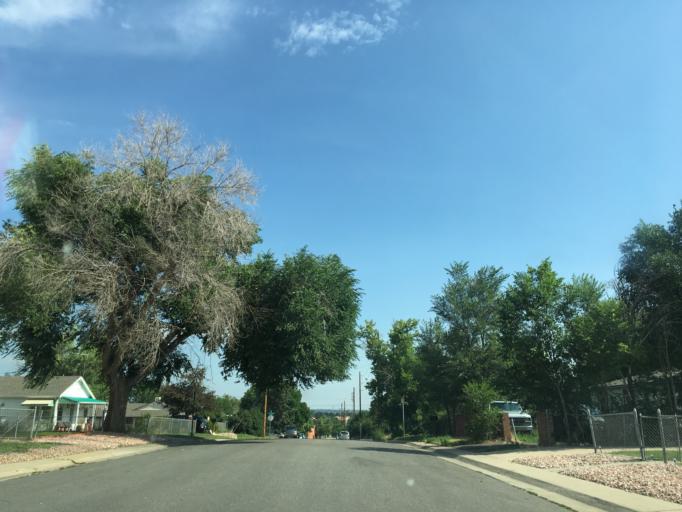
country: US
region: Colorado
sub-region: Jefferson County
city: Lakewood
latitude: 39.6977
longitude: -105.0426
